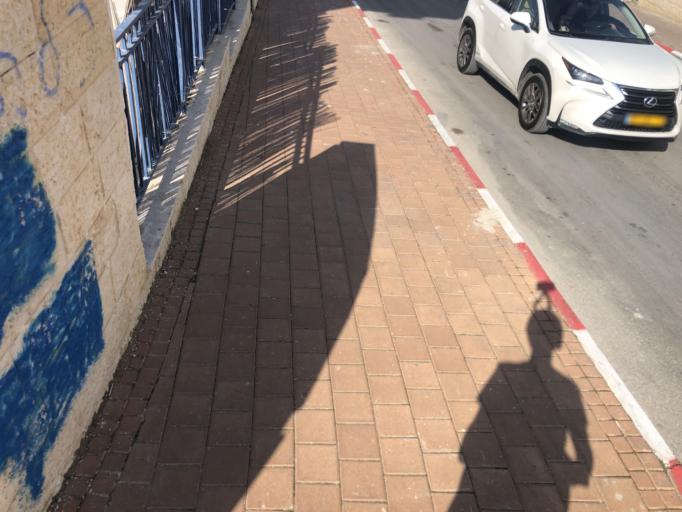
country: IL
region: Jerusalem
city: Modiin Ilit
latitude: 31.9232
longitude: 35.0539
